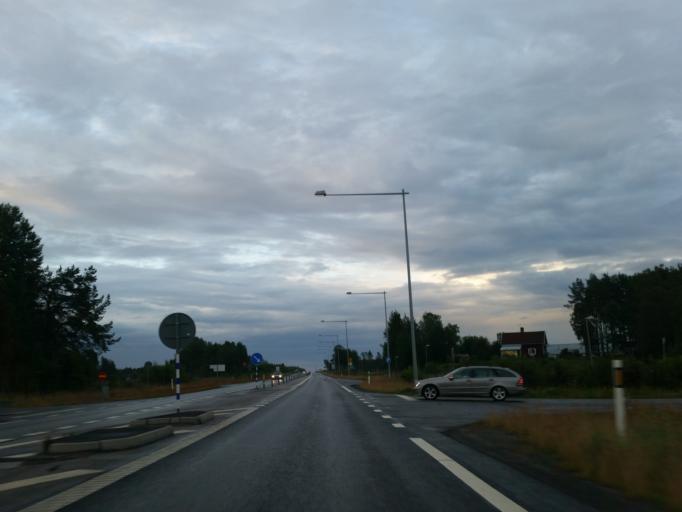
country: SE
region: Vaesterbotten
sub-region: Umea Kommun
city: Ersmark
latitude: 63.8555
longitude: 20.3871
